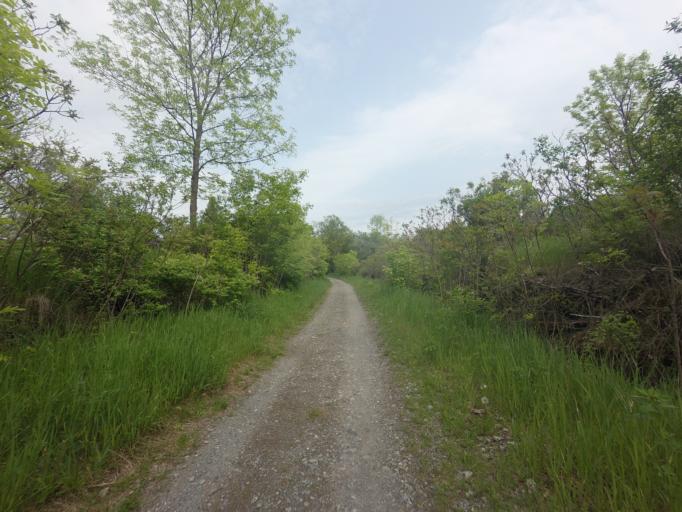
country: CA
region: Ontario
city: Kingston
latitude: 44.4097
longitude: -76.6060
